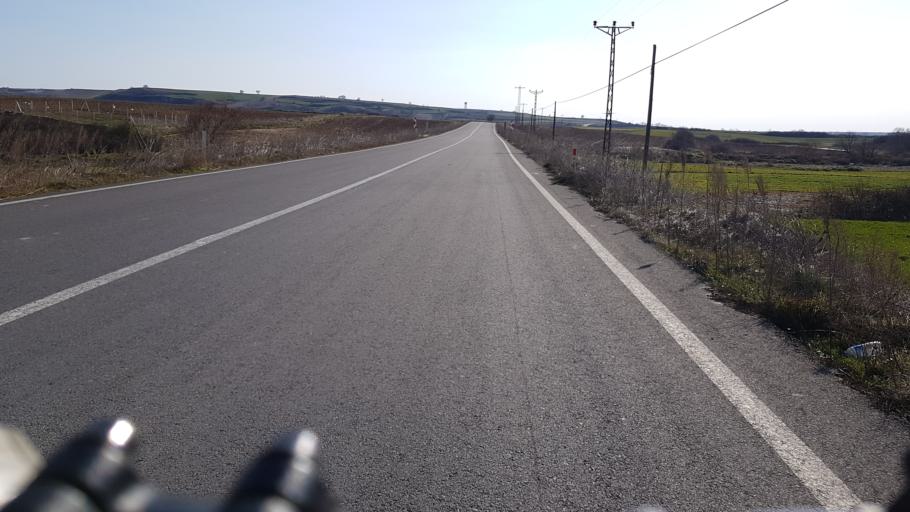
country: TR
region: Tekirdag
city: Saray
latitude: 41.3648
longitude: 27.8578
